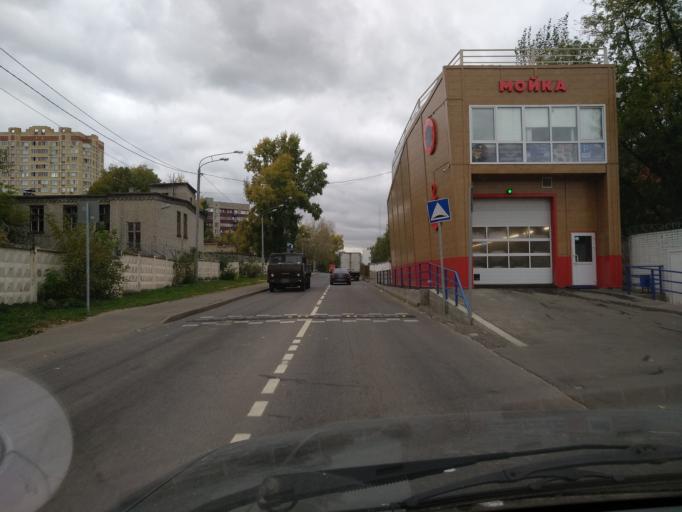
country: RU
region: Moskovskaya
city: Lyubertsy
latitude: 55.6710
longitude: 37.8840
